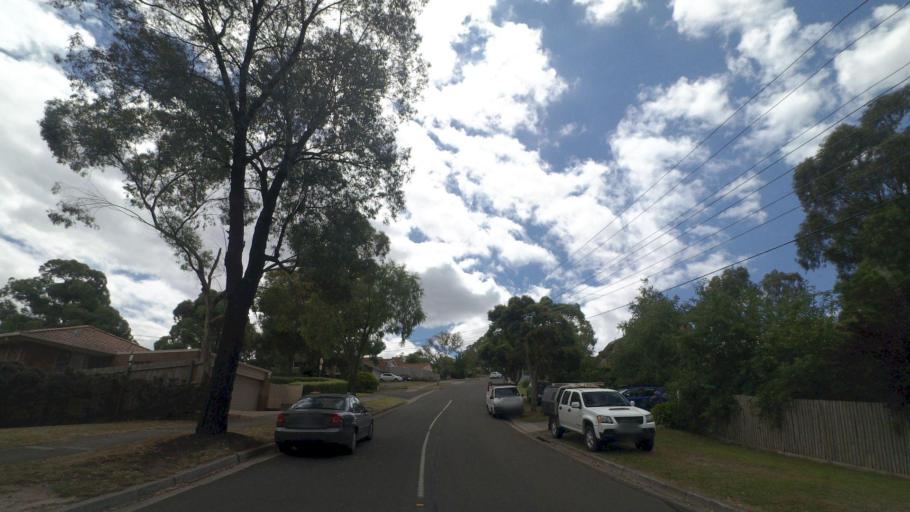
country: AU
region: Victoria
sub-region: Maroondah
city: Warranwood
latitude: -37.7766
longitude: 145.2406
